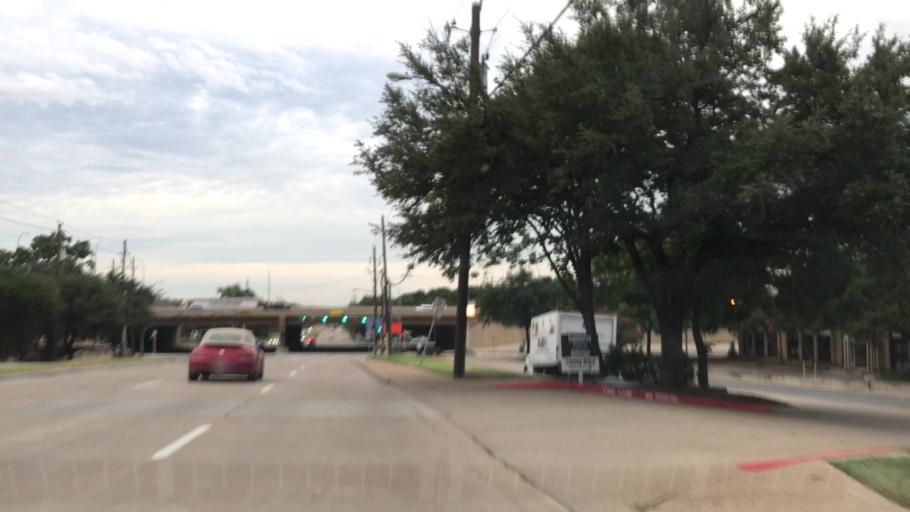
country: US
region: Texas
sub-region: Dallas County
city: Addison
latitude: 32.9229
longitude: -96.7861
